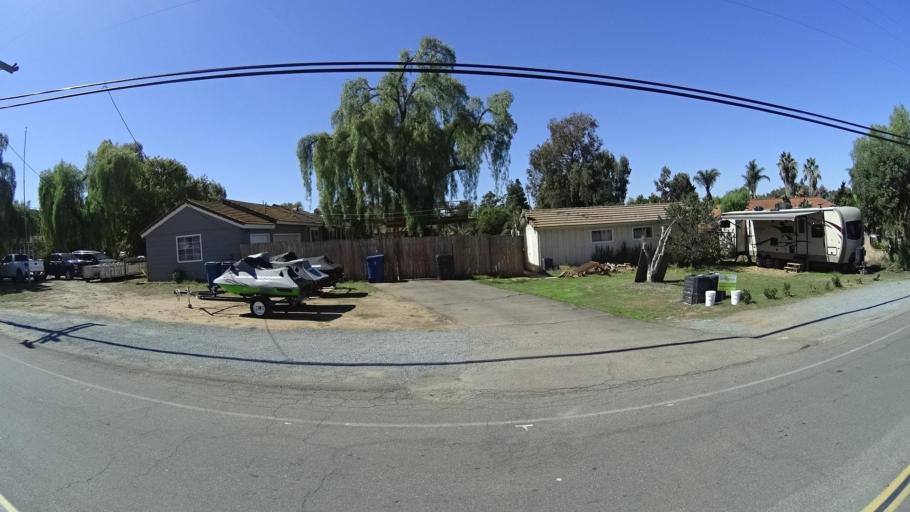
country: US
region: California
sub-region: San Diego County
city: Bonita
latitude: 32.6571
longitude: -117.0338
